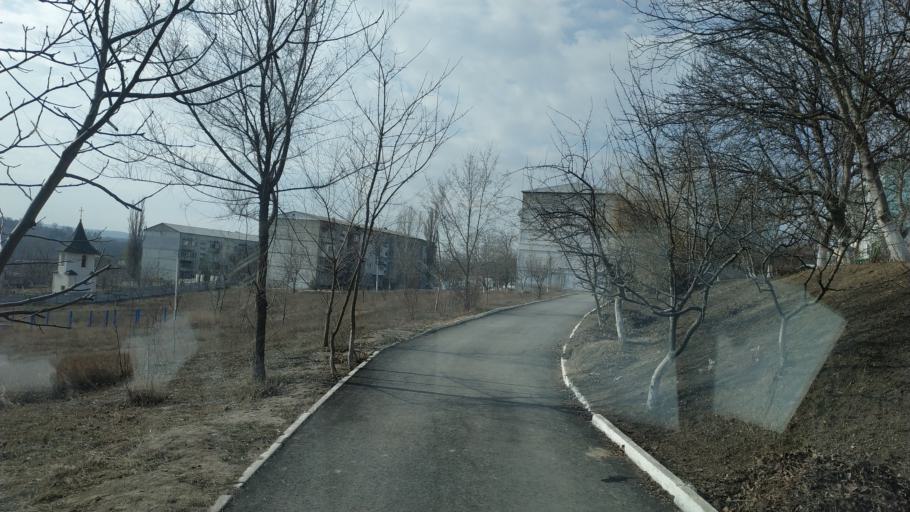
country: MD
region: Chisinau
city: Singera
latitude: 46.9269
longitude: 29.0688
